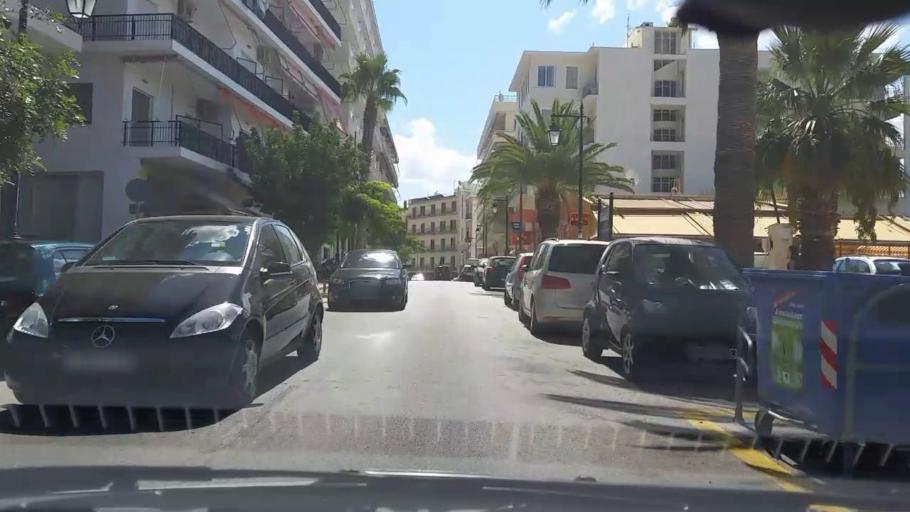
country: GR
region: Peloponnese
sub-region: Nomos Korinthias
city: Loutraki
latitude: 37.9818
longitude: 22.9728
